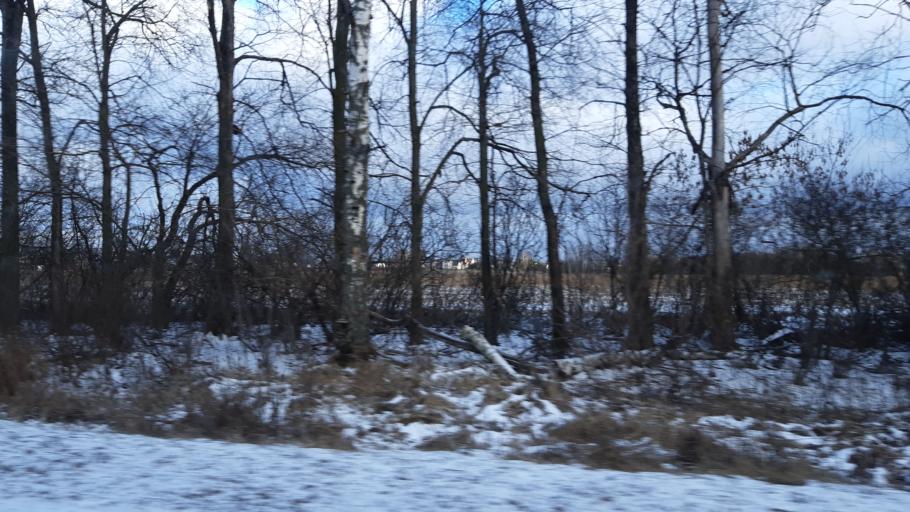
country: RU
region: Moskovskaya
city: Noginsk-9
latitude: 56.0117
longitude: 38.5587
